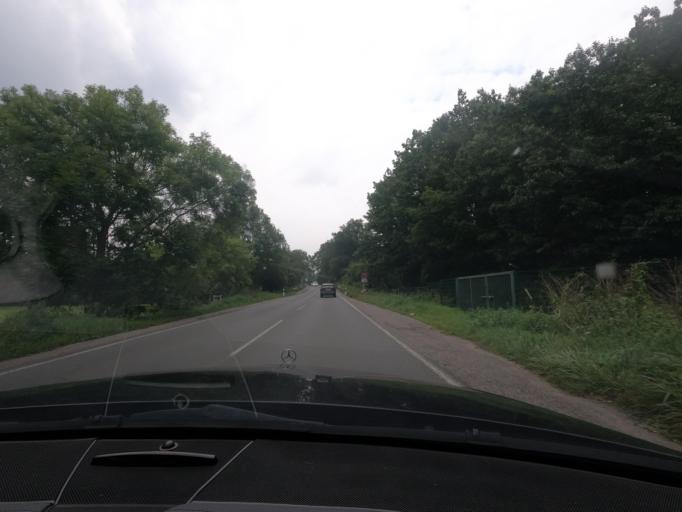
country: DE
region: North Rhine-Westphalia
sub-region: Regierungsbezirk Arnsberg
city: Holzwickede
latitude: 51.4546
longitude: 7.6270
